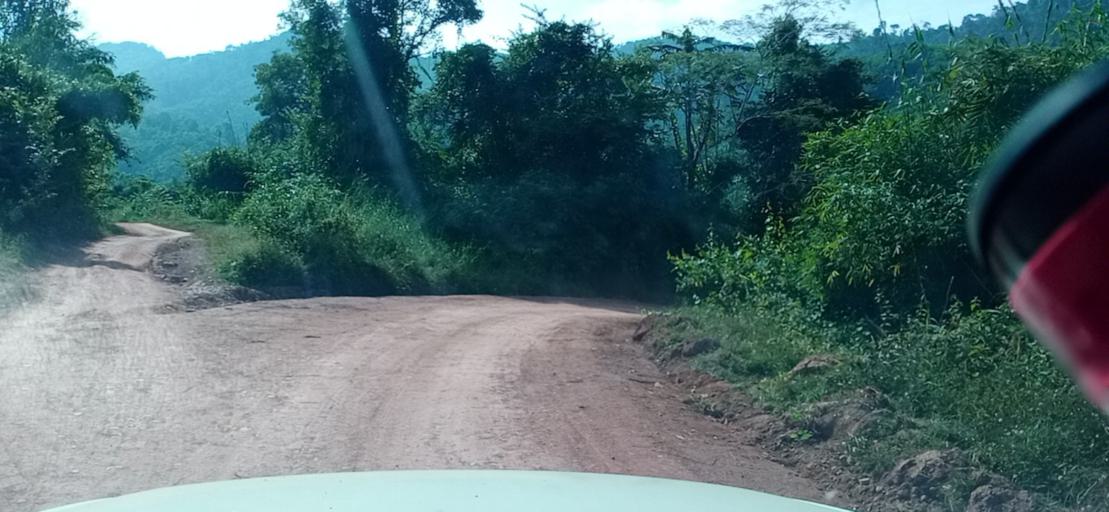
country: TH
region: Changwat Bueng Kan
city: Pak Khat
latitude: 18.6685
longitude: 103.2015
